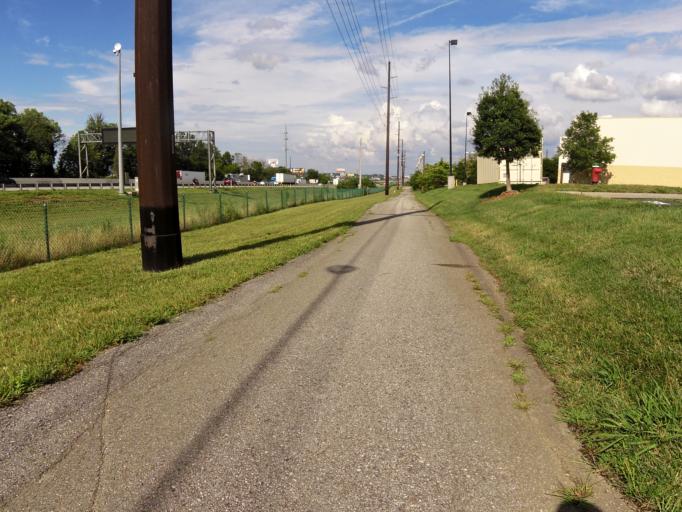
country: US
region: Tennessee
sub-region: Knox County
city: Farragut
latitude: 35.9024
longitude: -84.1584
